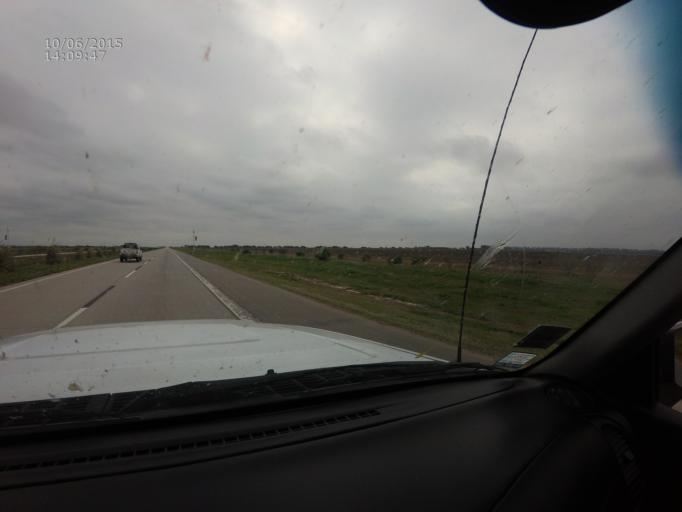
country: AR
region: Cordoba
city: Villa Maria
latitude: -32.4662
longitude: -63.0710
